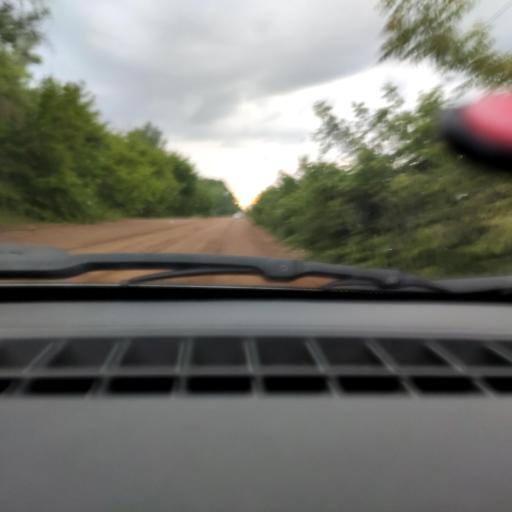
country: RU
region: Bashkortostan
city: Blagoveshchensk
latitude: 54.9141
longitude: 55.9909
